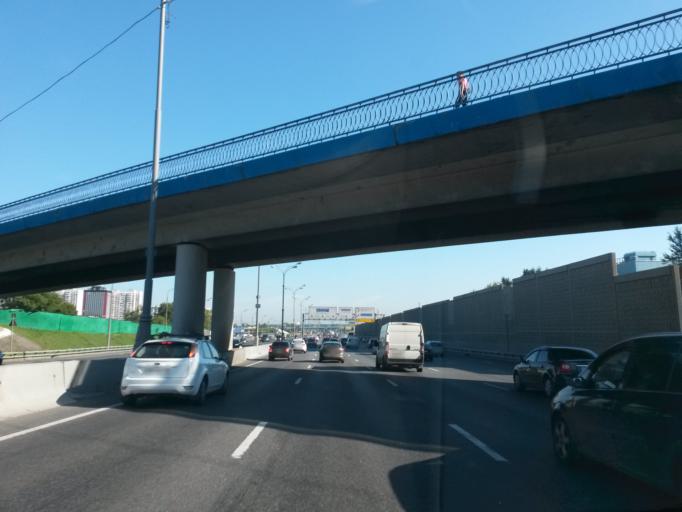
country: RU
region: Moscow
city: Vostochnyy
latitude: 55.8072
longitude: 37.8398
